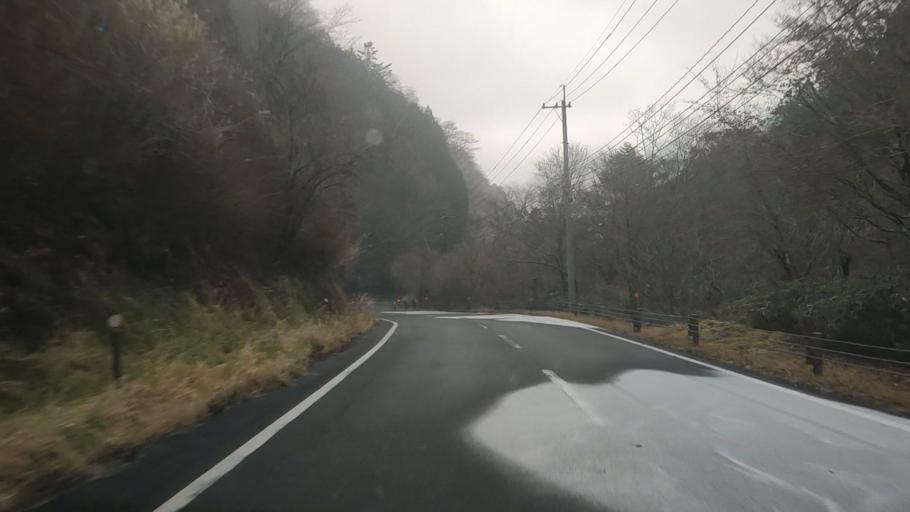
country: JP
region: Kumamoto
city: Matsubase
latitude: 32.5630
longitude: 130.9141
